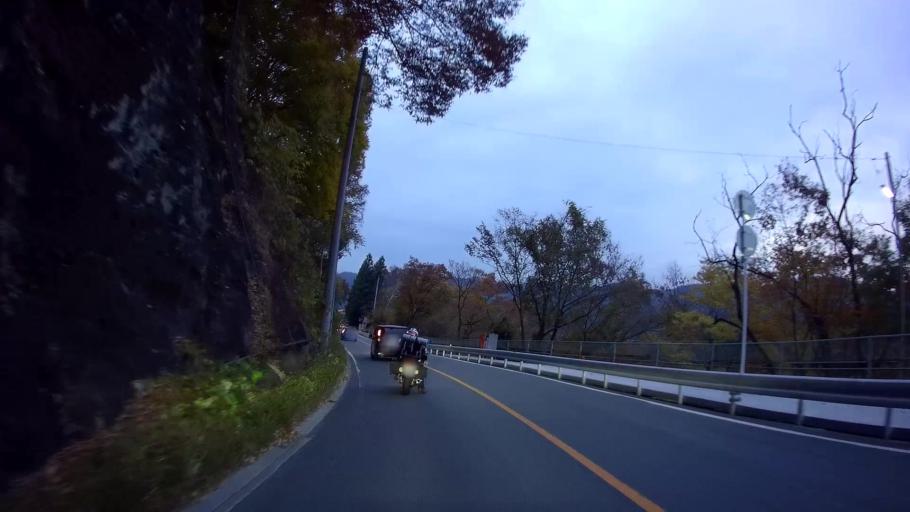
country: JP
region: Gunma
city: Nakanojomachi
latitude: 36.5499
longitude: 138.7931
